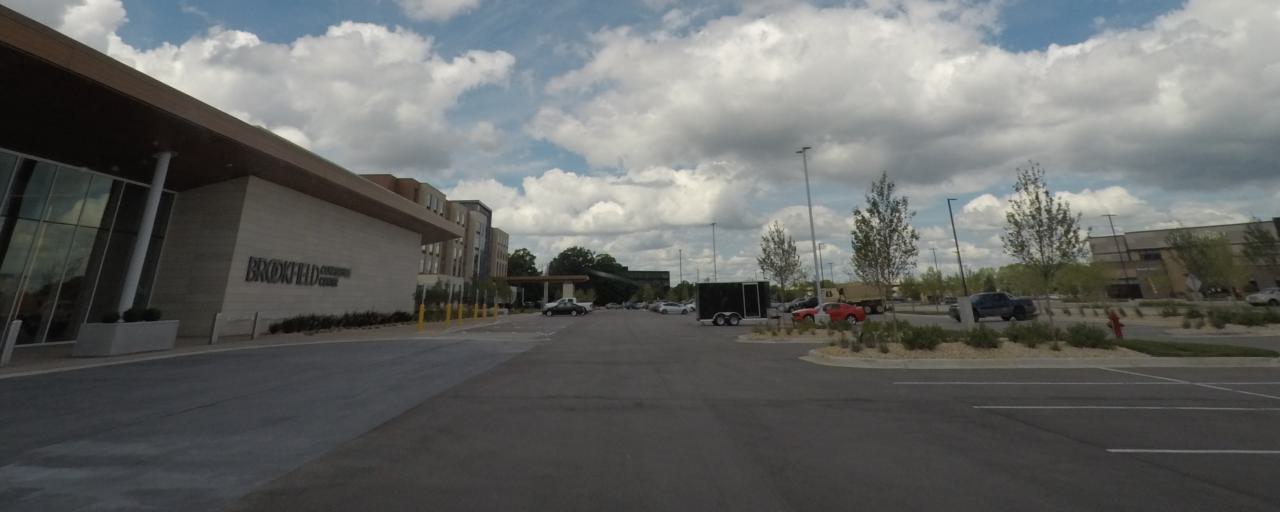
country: US
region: Wisconsin
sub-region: Waukesha County
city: Brookfield
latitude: 43.0288
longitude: -88.1095
